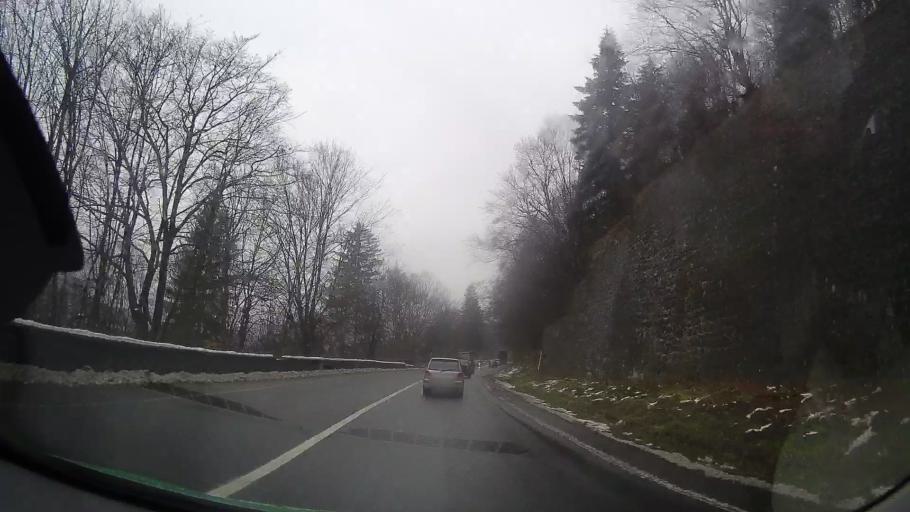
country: RO
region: Neamt
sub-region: Comuna Tarcau
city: Tarcau
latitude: 46.8988
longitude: 26.1198
